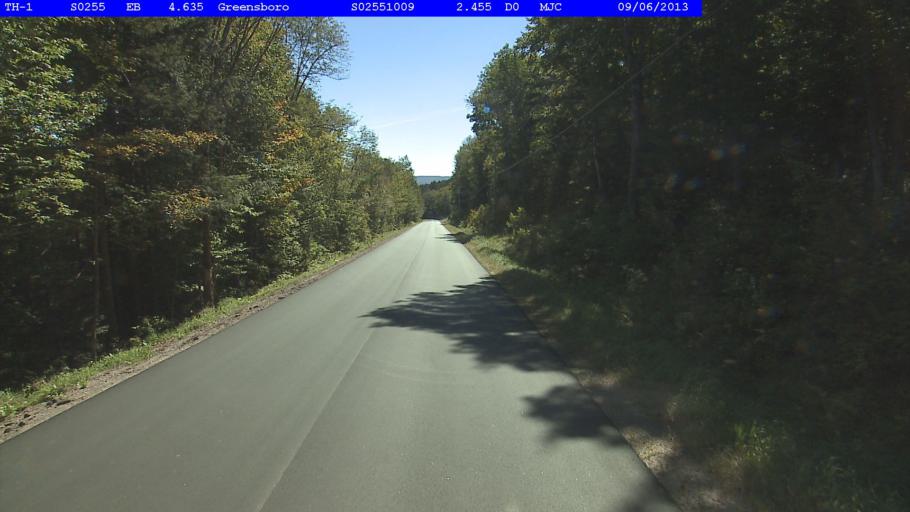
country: US
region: Vermont
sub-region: Caledonia County
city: Hardwick
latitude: 44.6080
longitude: -72.3179
